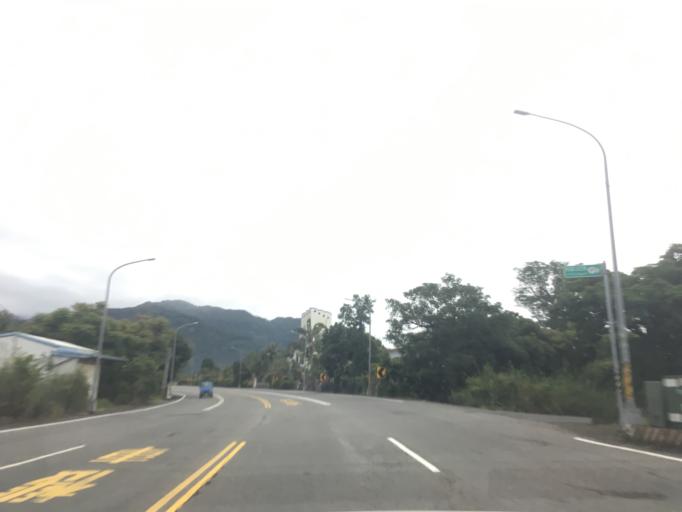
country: TW
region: Taiwan
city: Taitung City
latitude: 22.7459
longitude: 121.0570
